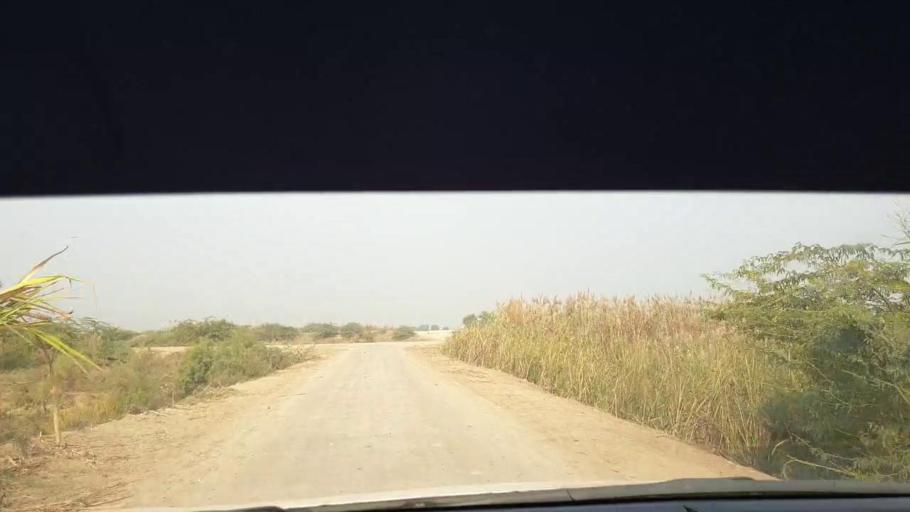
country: PK
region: Sindh
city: Berani
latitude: 25.8473
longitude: 68.8472
